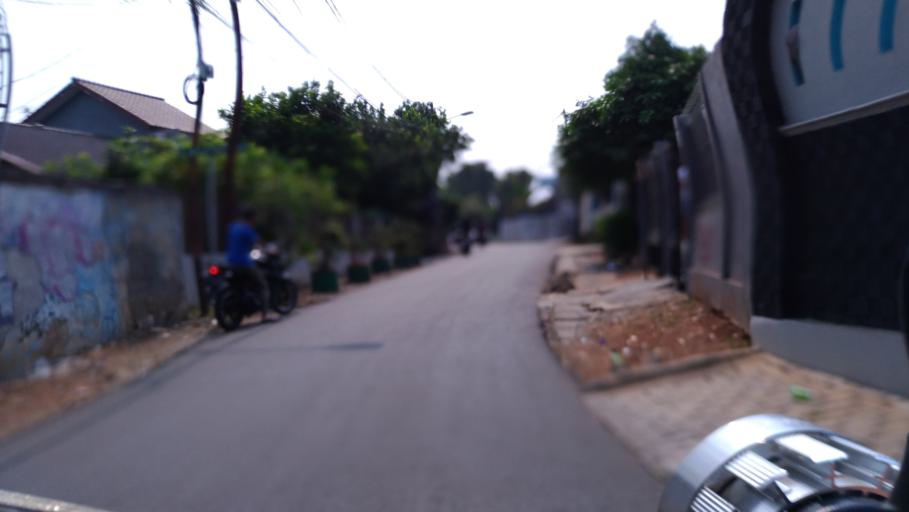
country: ID
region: West Java
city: Depok
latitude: -6.3549
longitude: 106.8741
